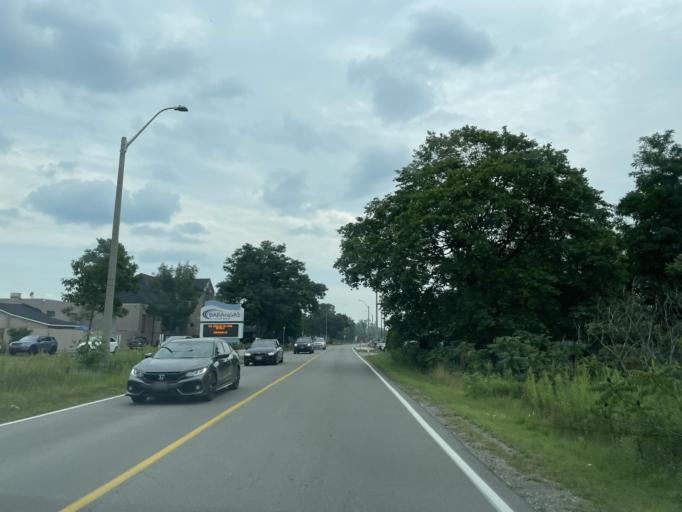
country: CA
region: Ontario
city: Hamilton
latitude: 43.2560
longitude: -79.7627
